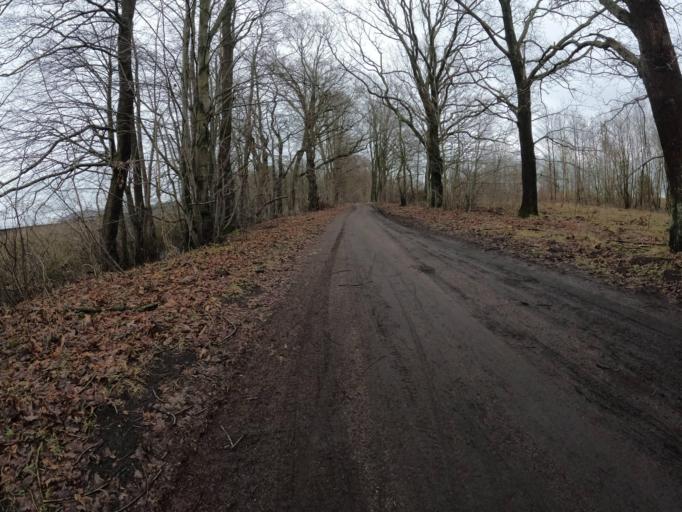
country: PL
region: West Pomeranian Voivodeship
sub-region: Powiat slawienski
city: Darlowo
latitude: 54.4062
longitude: 16.4398
